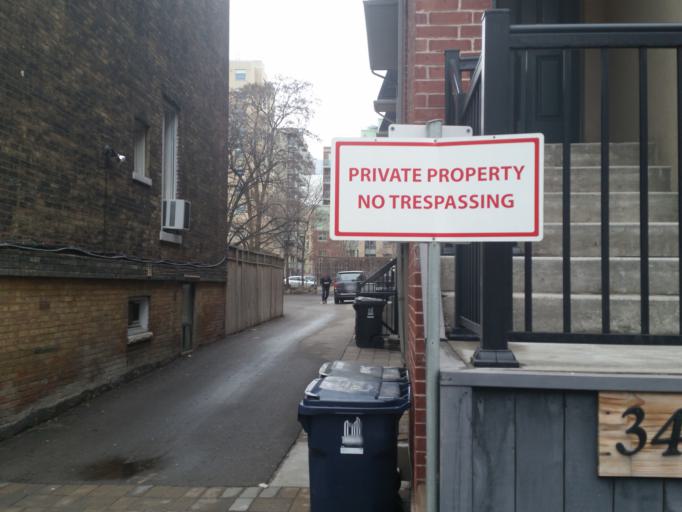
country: CA
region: Ontario
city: Toronto
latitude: 43.6630
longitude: -79.3770
